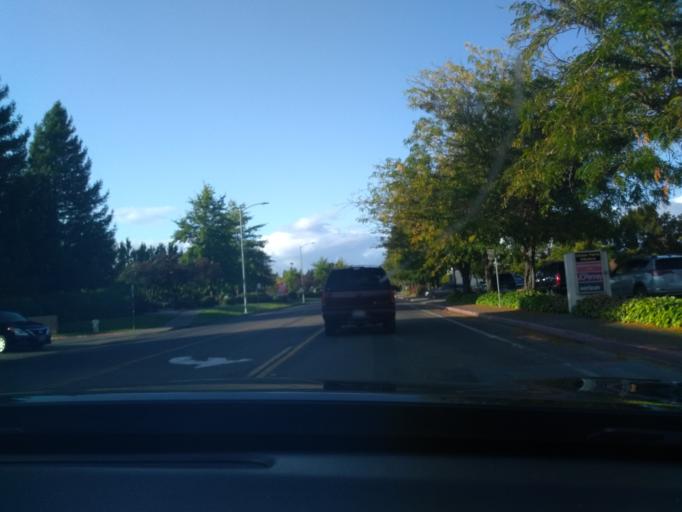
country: US
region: California
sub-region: Mendocino County
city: Ukiah
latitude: 39.1534
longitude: -123.1991
